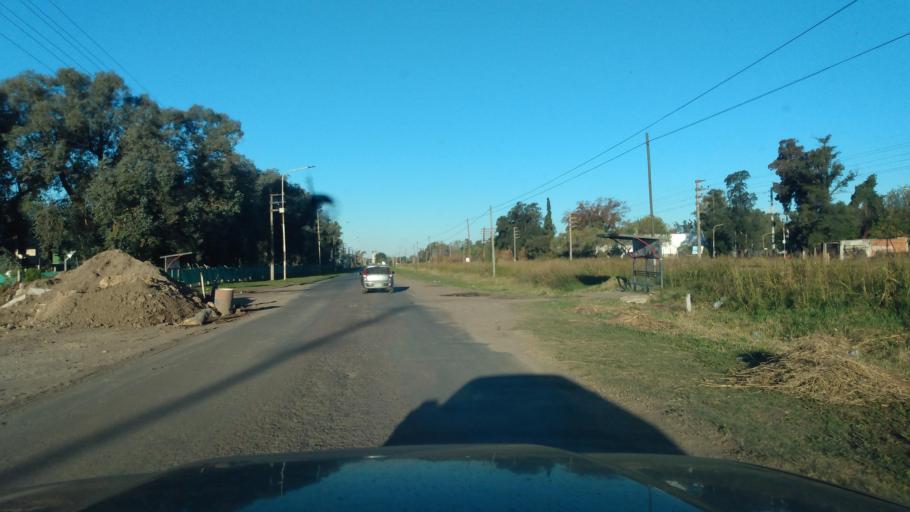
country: AR
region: Buenos Aires
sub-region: Partido de General Rodriguez
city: General Rodriguez
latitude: -34.6266
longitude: -58.8760
